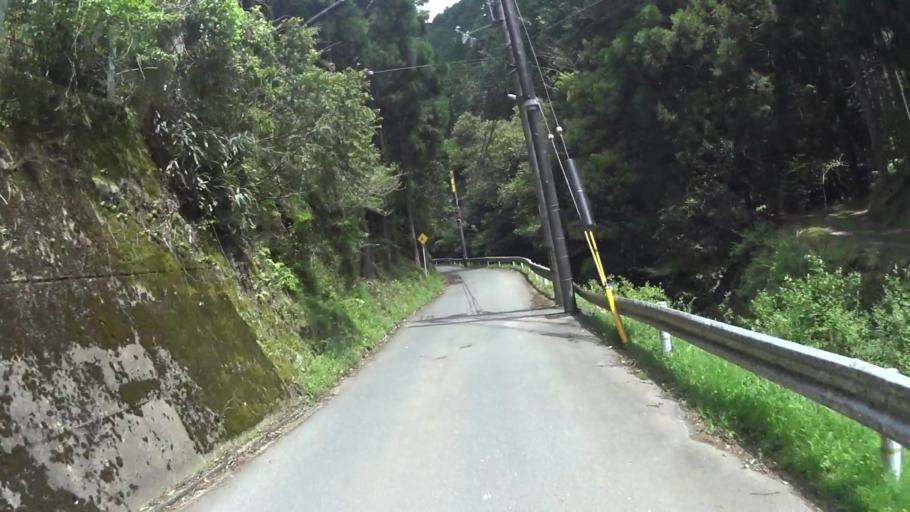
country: JP
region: Kyoto
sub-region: Kyoto-shi
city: Kamigyo-ku
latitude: 35.1008
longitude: 135.7035
